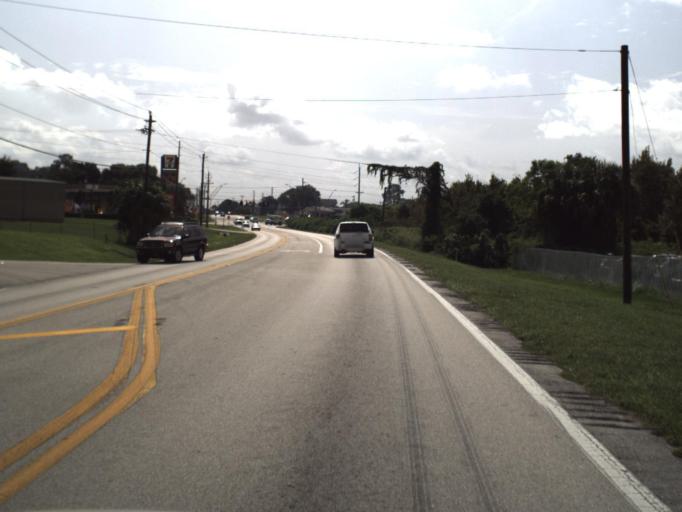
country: US
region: Florida
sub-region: Polk County
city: Jan-Phyl Village
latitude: 28.0278
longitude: -81.7782
